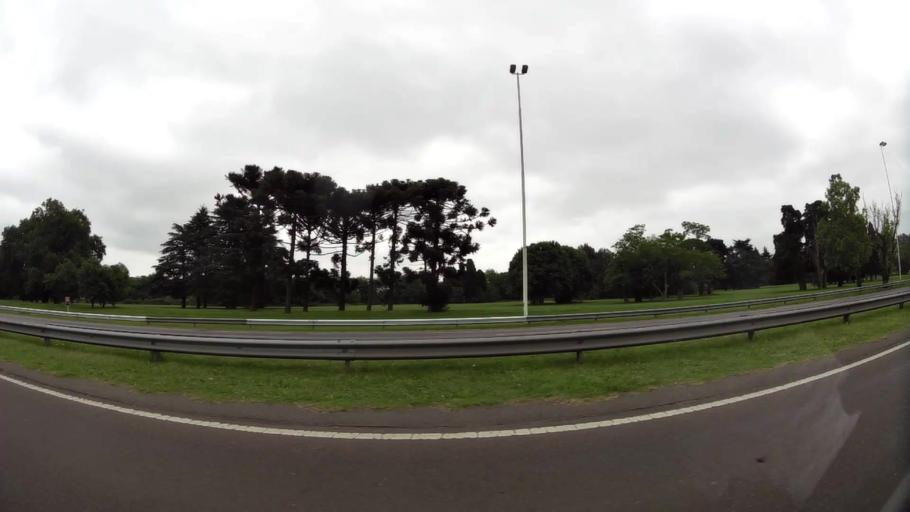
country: AR
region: Buenos Aires
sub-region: Partido de Ezeiza
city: Ezeiza
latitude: -34.7960
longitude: -58.5309
